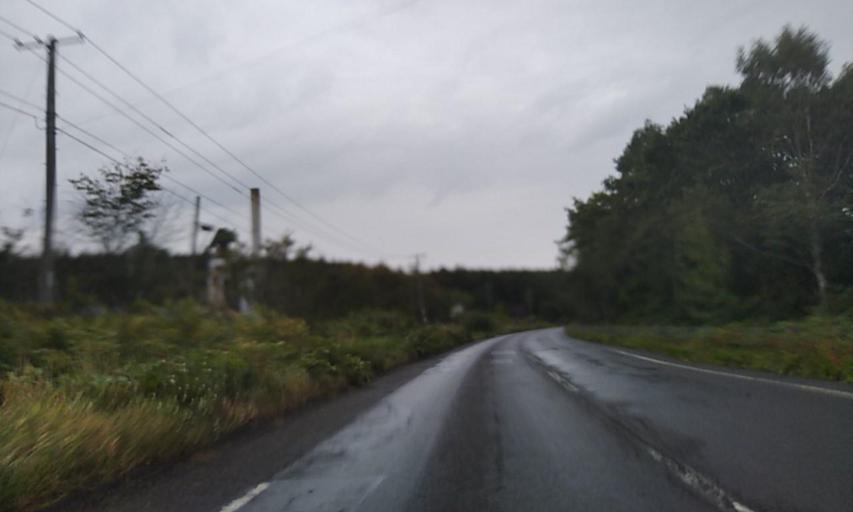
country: JP
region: Hokkaido
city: Mombetsu
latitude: 44.4821
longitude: 143.1030
